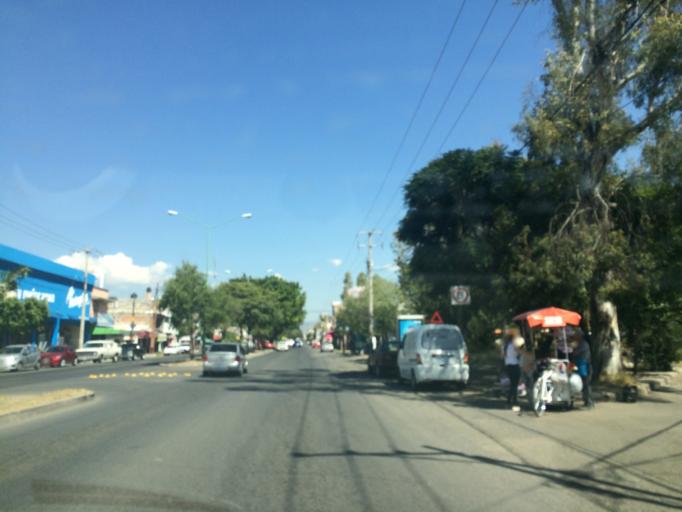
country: MX
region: Guanajuato
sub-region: Leon
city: San Jose de Duran (Los Troncoso)
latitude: 21.0873
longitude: -101.6487
